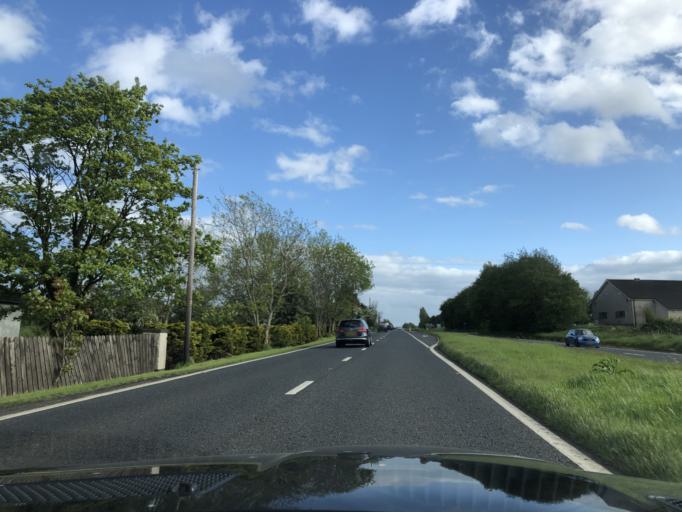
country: GB
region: Northern Ireland
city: Cullybackey
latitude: 54.9411
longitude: -6.3300
